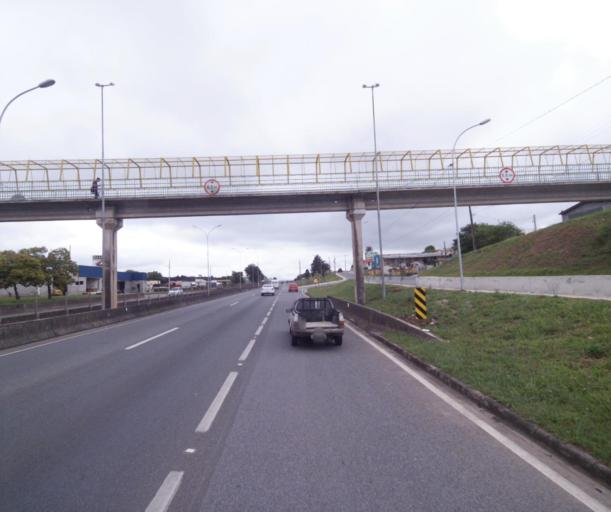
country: BR
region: Parana
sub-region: Quatro Barras
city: Quatro Barras
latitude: -25.3679
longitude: -49.1059
